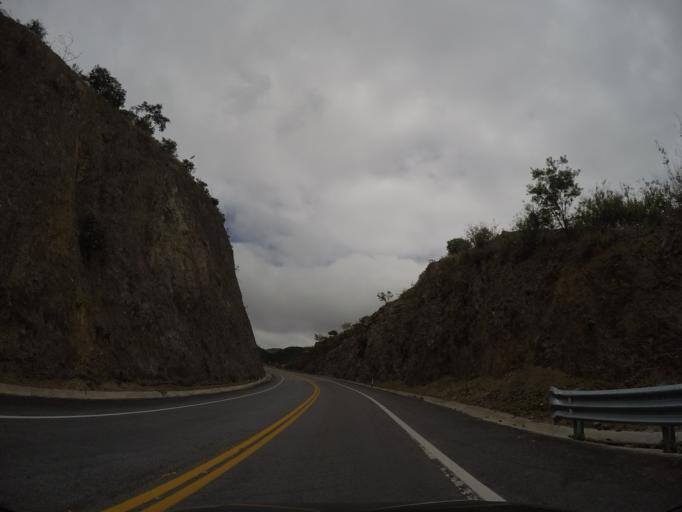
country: MX
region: Oaxaca
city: San Lorenzo Albarradas
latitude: 16.9363
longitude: -96.2665
